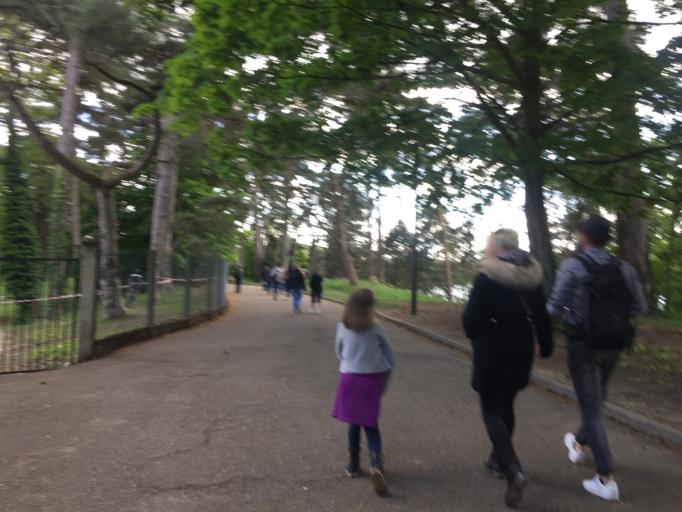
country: FR
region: Rhone-Alpes
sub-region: Departement du Rhone
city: Caluire-et-Cuire
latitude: 45.7823
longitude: 4.8552
